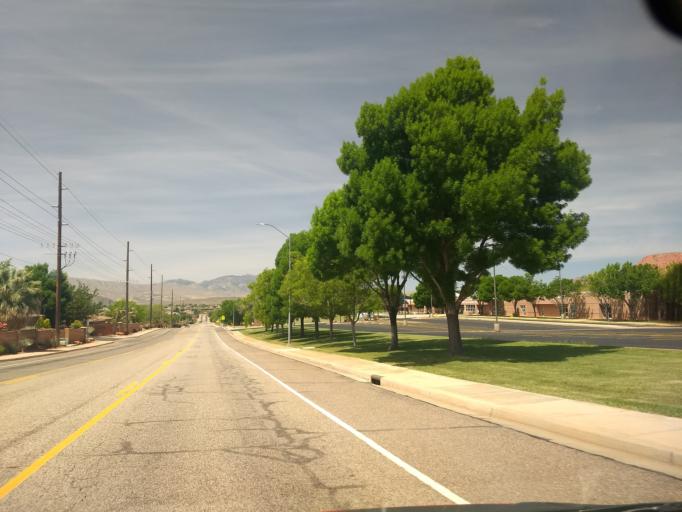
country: US
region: Utah
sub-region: Washington County
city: Santa Clara
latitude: 37.1431
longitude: -113.6254
